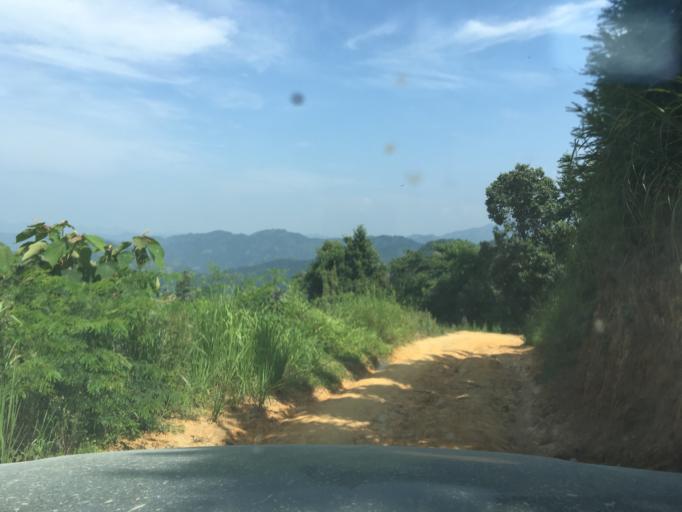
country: CN
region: Guangxi Zhuangzu Zizhiqu
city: Xinzhou
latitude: 25.0448
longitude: 105.8672
